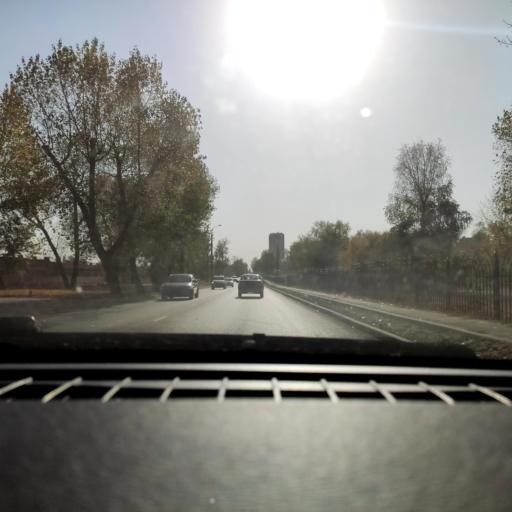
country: RU
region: Voronezj
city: Voronezh
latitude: 51.6596
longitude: 39.2499
